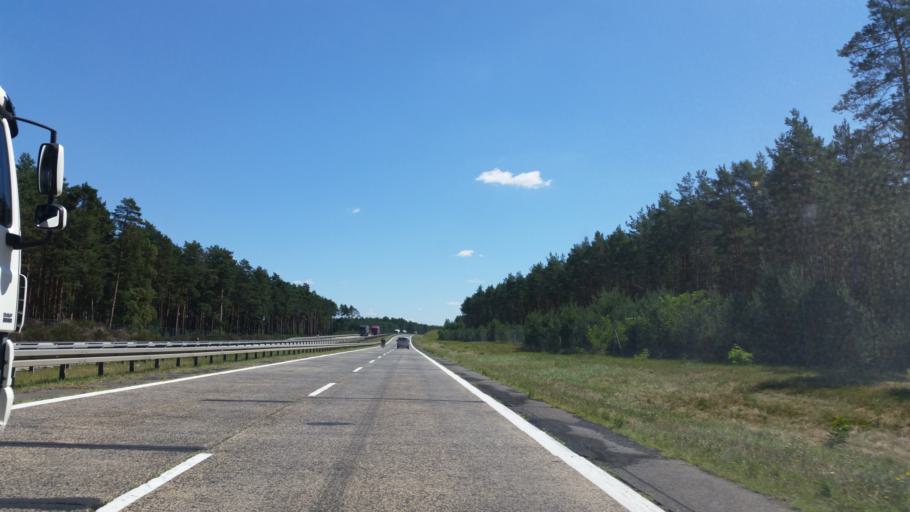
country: PL
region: Lubusz
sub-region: Powiat zaganski
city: Malomice
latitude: 51.4203
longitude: 15.4683
